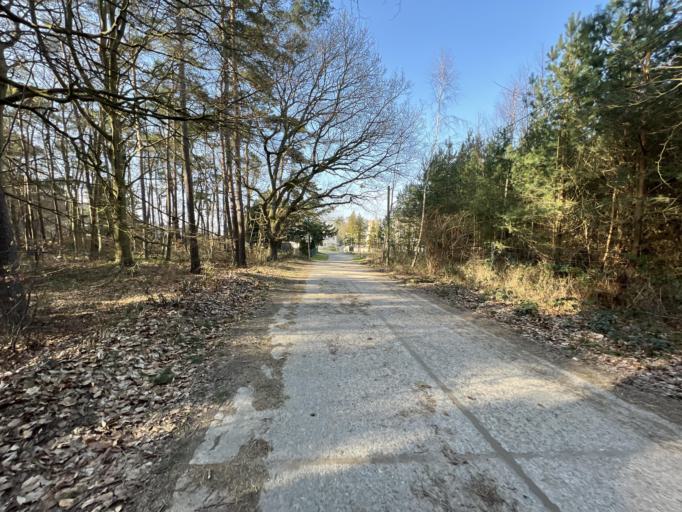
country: DE
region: Mecklenburg-Vorpommern
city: Sagard
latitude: 54.4817
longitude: 13.5635
